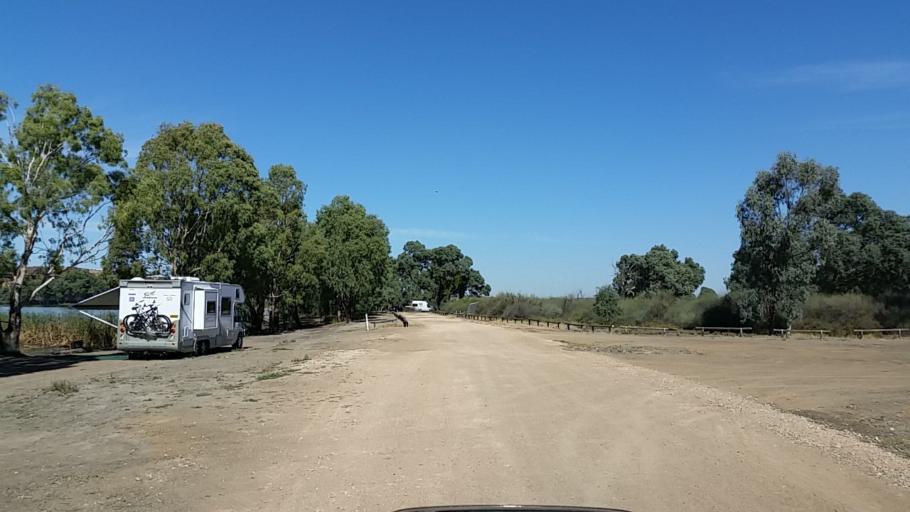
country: AU
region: South Australia
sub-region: Mid Murray
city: Mannum
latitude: -34.7002
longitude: 139.5761
